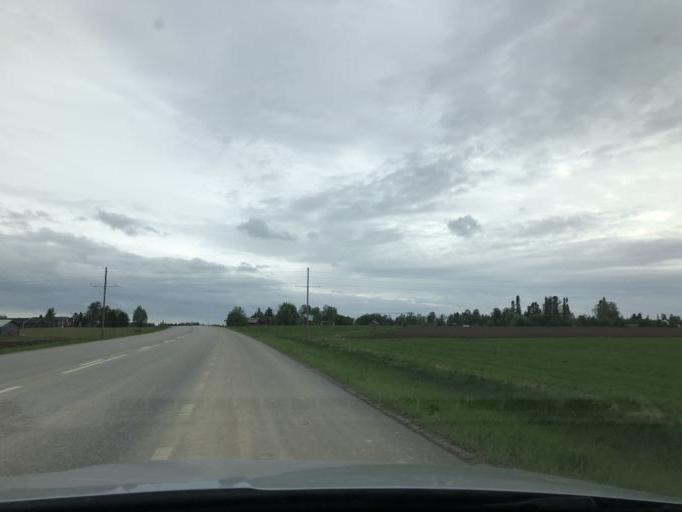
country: SE
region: Norrbotten
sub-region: Pitea Kommun
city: Bergsviken
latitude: 65.3597
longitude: 21.4028
